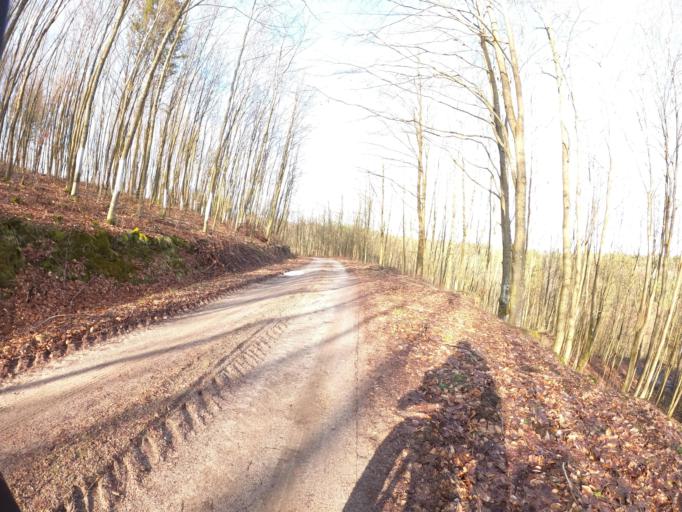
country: PL
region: West Pomeranian Voivodeship
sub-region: Powiat koszalinski
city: Polanow
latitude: 54.2238
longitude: 16.6888
